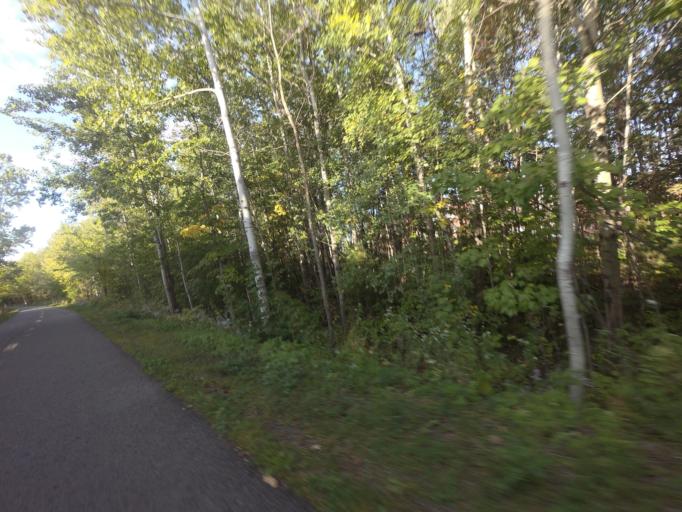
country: CA
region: Quebec
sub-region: Laurentides
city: Saint-Jerome
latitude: 45.7919
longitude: -73.9971
